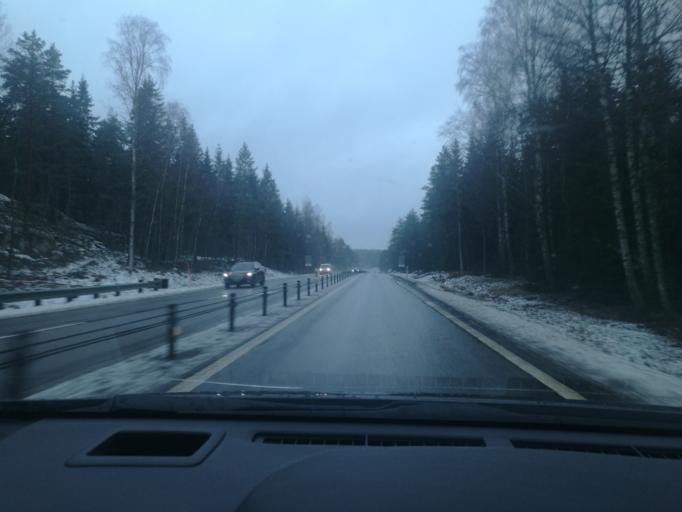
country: SE
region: OEstergoetland
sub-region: Norrkopings Kommun
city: Jursla
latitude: 58.7316
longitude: 16.1733
